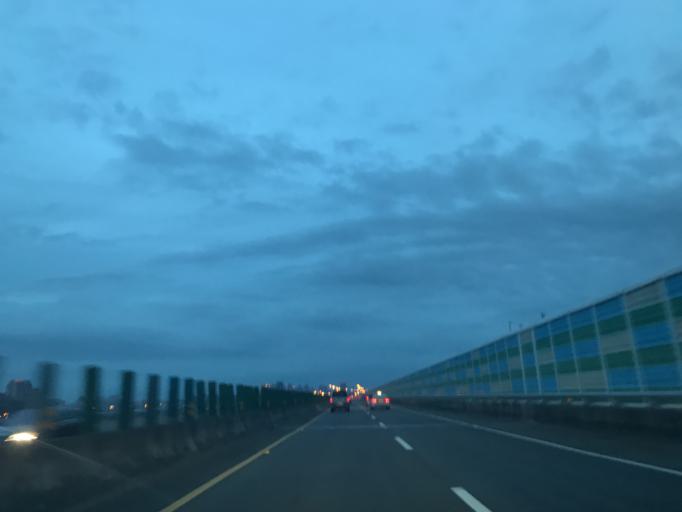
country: TW
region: Taiwan
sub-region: Hsinchu
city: Hsinchu
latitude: 24.8225
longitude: 120.9857
